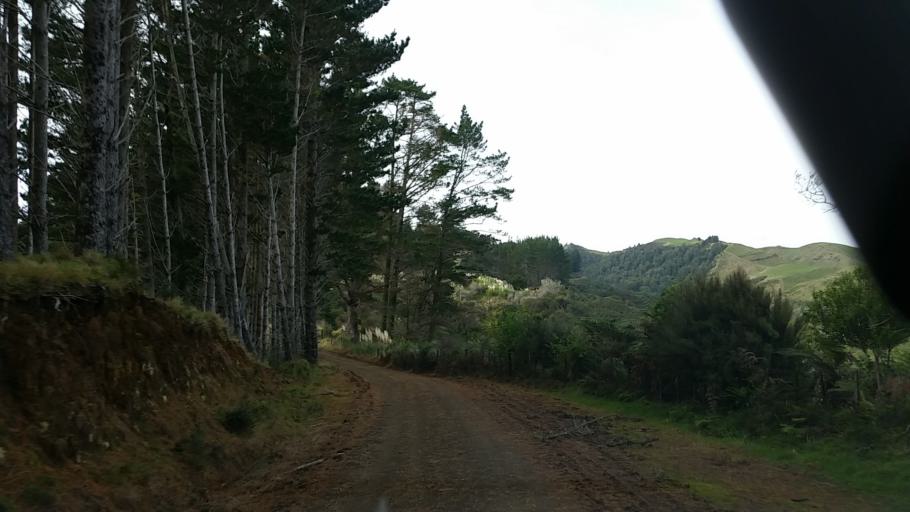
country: NZ
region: Taranaki
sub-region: New Plymouth District
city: Waitara
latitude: -39.0411
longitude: 174.4191
